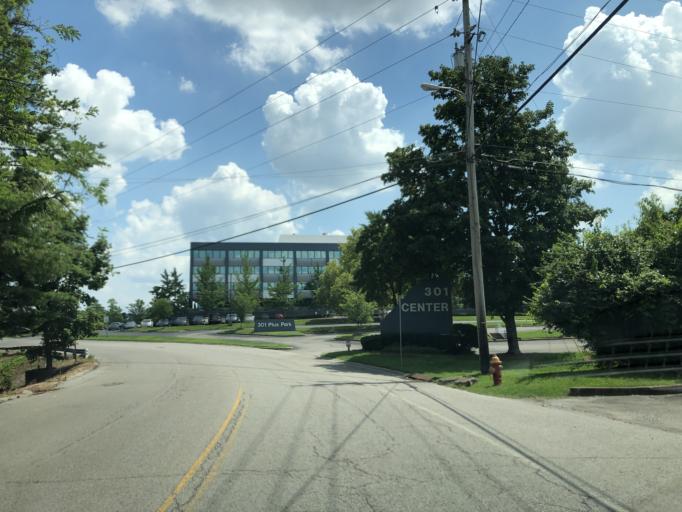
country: US
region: Tennessee
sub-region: Davidson County
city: Nashville
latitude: 36.1291
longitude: -86.7257
